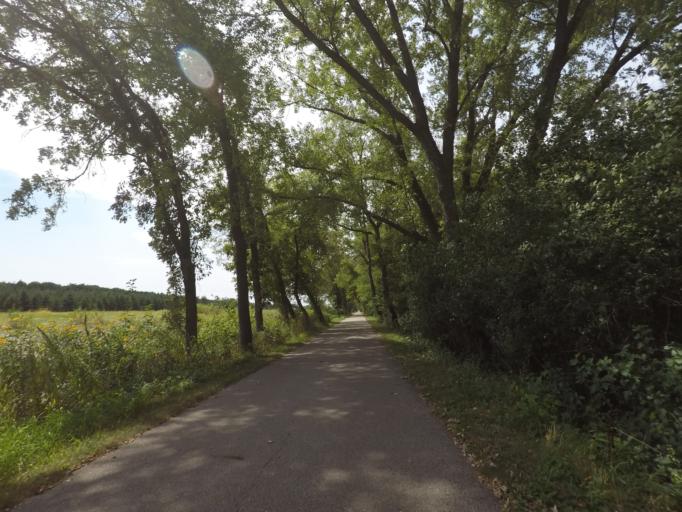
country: US
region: Wisconsin
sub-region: Jefferson County
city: Lake Koshkonong
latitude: 42.8572
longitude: -88.9060
